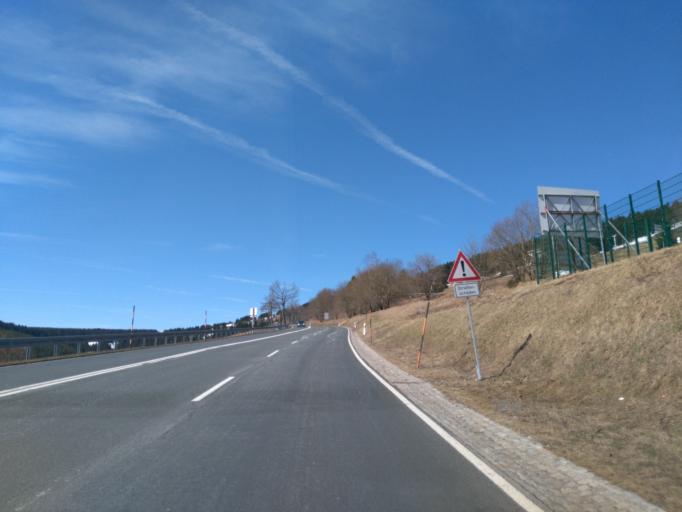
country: DE
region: Saxony
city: Kurort Oberwiesenthal
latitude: 50.4173
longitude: 12.9601
